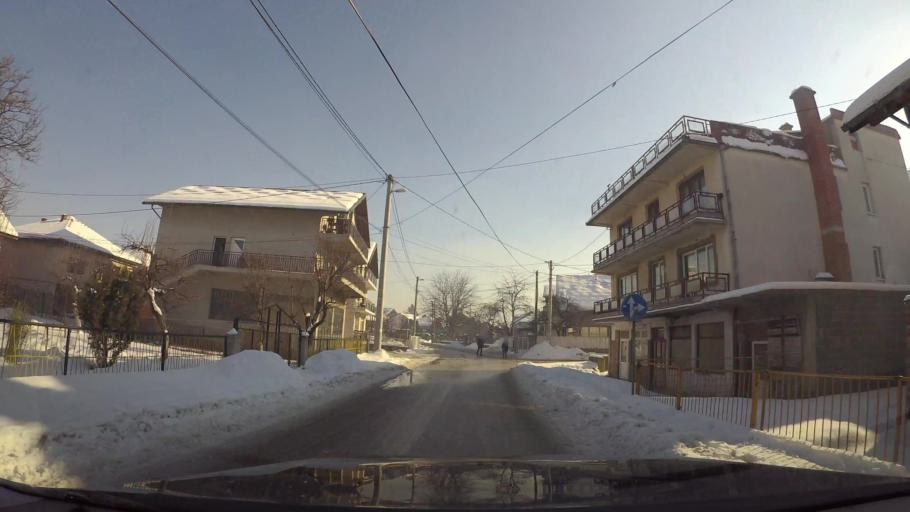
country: BA
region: Federation of Bosnia and Herzegovina
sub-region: Kanton Sarajevo
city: Sarajevo
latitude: 43.8157
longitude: 18.3125
